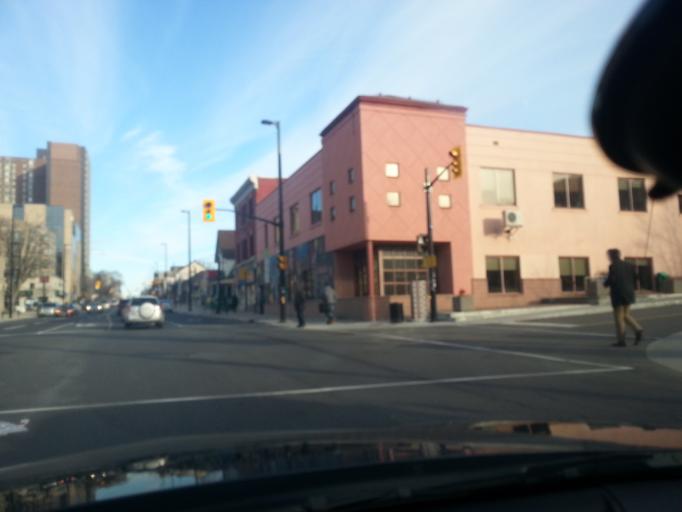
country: CA
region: Ontario
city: Ottawa
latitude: 45.4293
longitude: -75.6843
